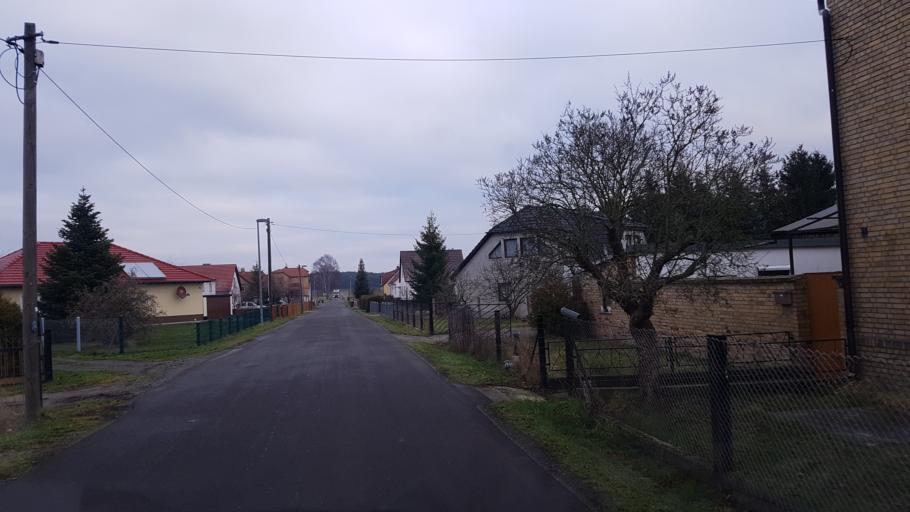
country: DE
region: Brandenburg
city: Schipkau
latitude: 51.5447
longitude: 13.8979
